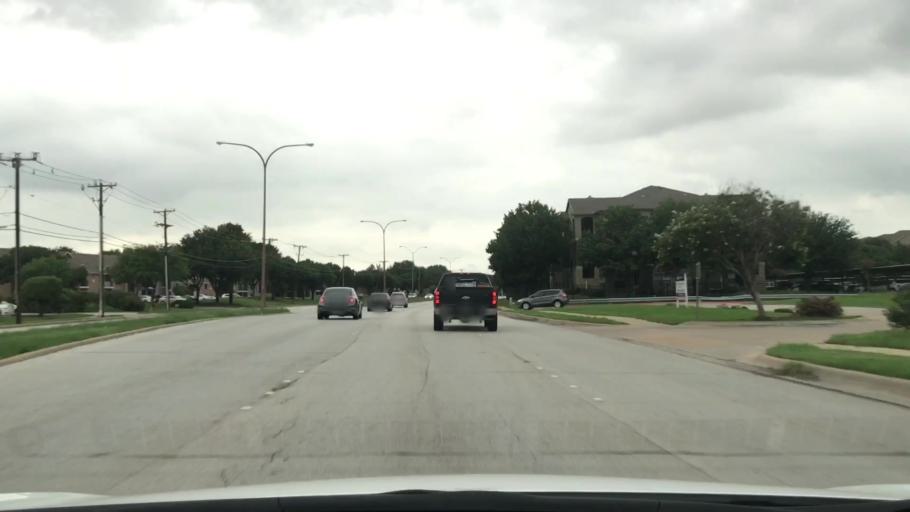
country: US
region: Texas
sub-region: Tarrant County
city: Watauga
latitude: 32.8628
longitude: -97.2903
